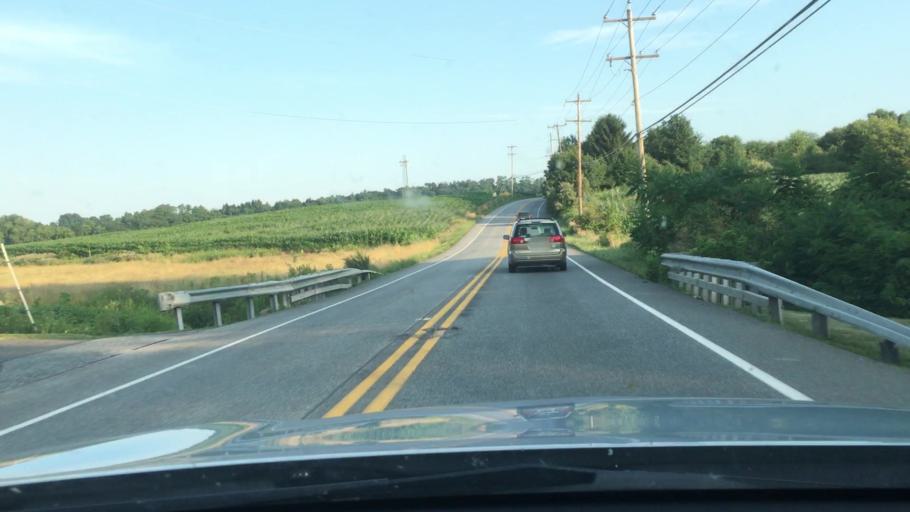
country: US
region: Pennsylvania
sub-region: York County
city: Dillsburg
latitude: 40.1283
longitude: -77.0373
